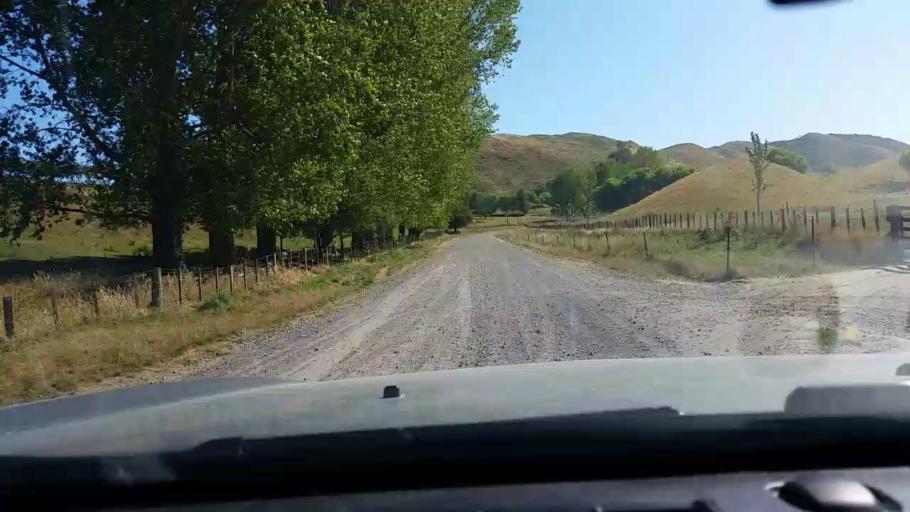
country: NZ
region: Bay of Plenty
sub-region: Rotorua District
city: Rotorua
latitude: -38.3095
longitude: 176.3050
